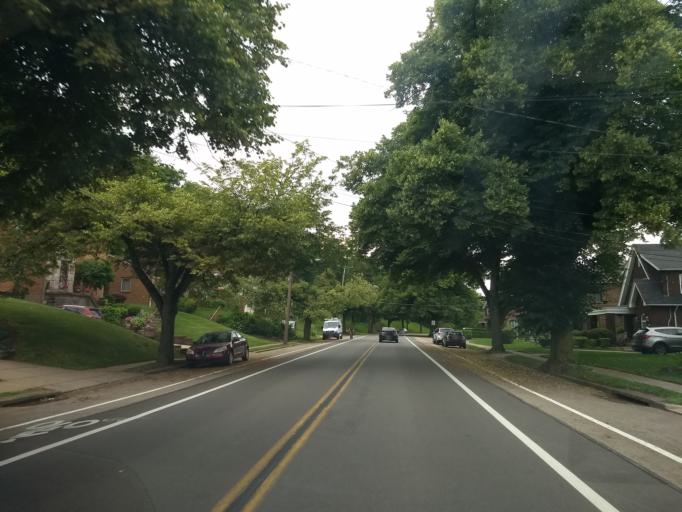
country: US
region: Pennsylvania
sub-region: Allegheny County
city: Homestead
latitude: 40.4226
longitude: -79.9181
